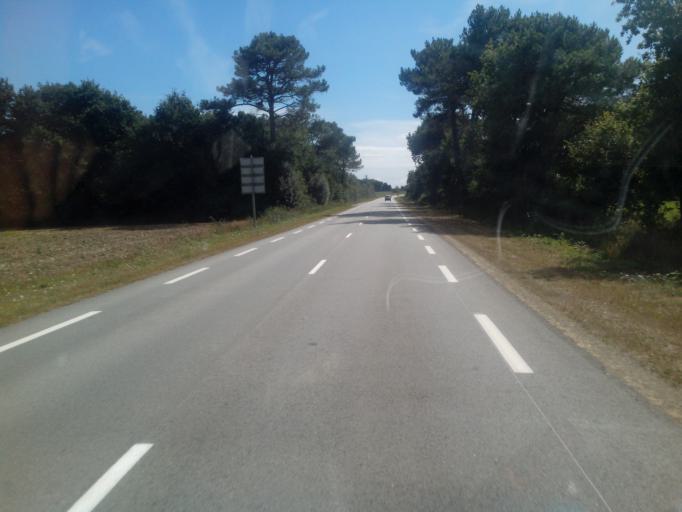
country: FR
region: Brittany
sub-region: Departement du Morbihan
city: Peaule
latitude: 47.5537
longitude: -2.3962
